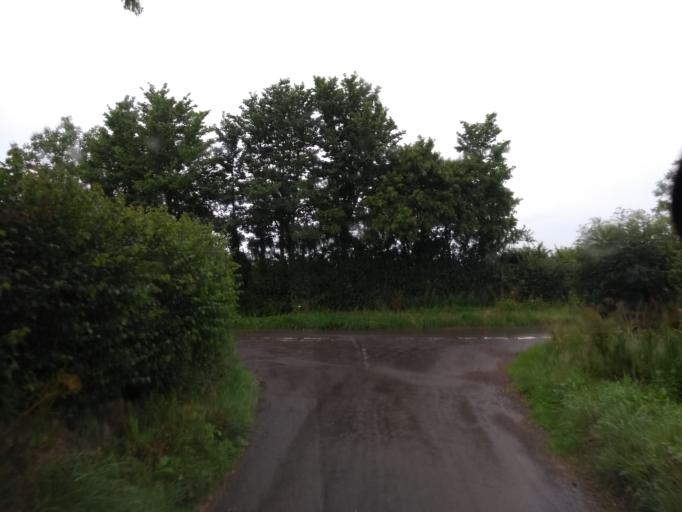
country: GB
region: England
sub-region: Somerset
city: Street
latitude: 51.0983
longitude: -2.6991
